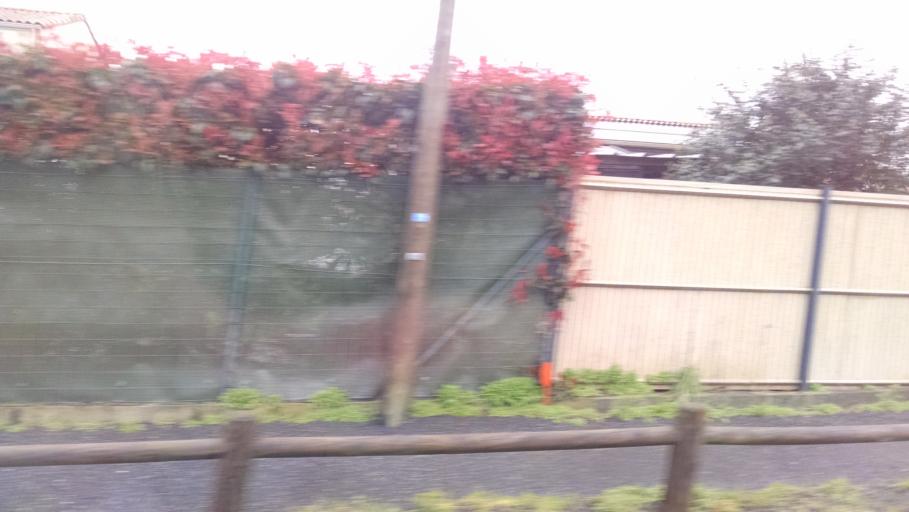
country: FR
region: Pays de la Loire
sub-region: Departement de la Loire-Atlantique
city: Aigrefeuille-sur-Maine
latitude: 47.0834
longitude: -1.4050
